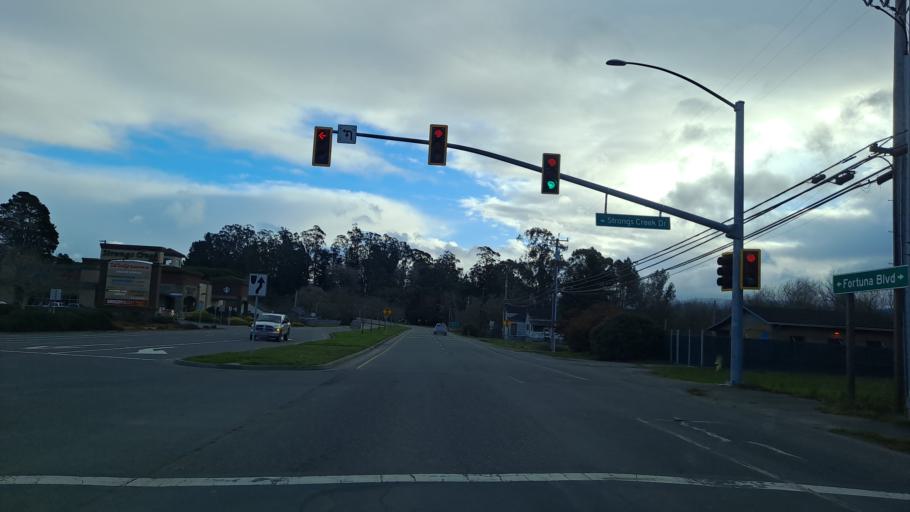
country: US
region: California
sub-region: Humboldt County
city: Fortuna
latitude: 40.5800
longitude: -124.1469
